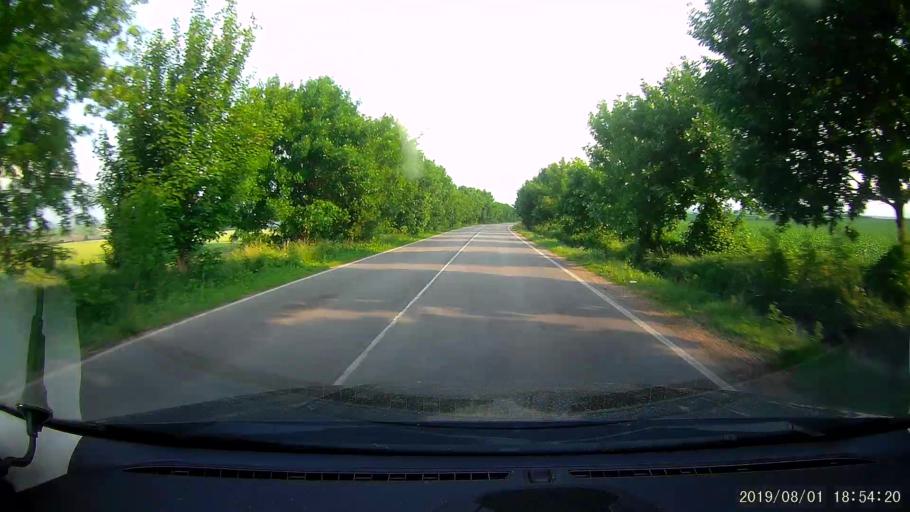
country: BG
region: Shumen
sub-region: Obshtina Shumen
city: Shumen
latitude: 43.2012
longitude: 27.0012
